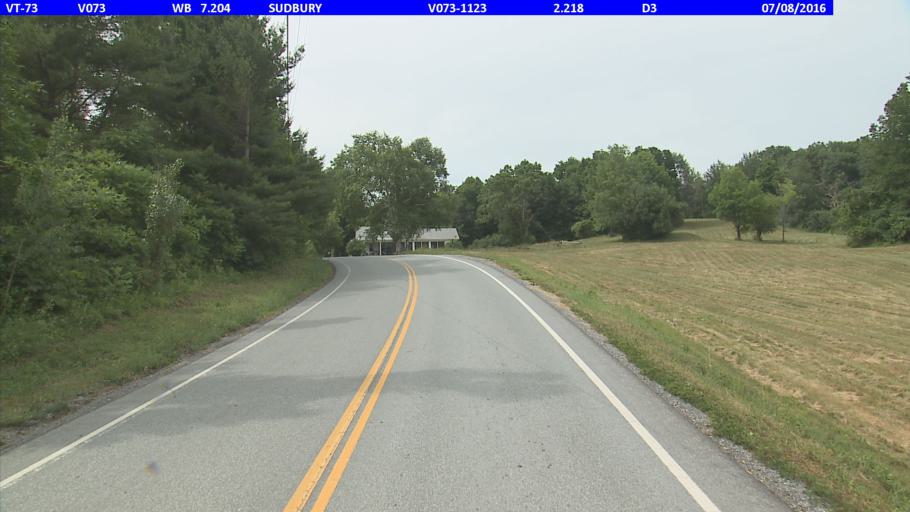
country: US
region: Vermont
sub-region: Rutland County
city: Brandon
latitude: 43.8157
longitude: -73.1616
